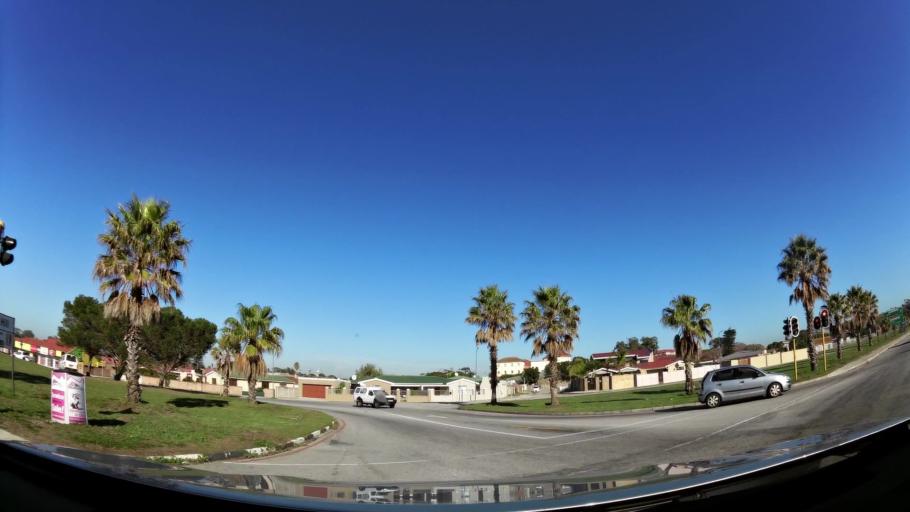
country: ZA
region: Eastern Cape
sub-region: Nelson Mandela Bay Metropolitan Municipality
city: Port Elizabeth
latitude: -33.9798
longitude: 25.6294
